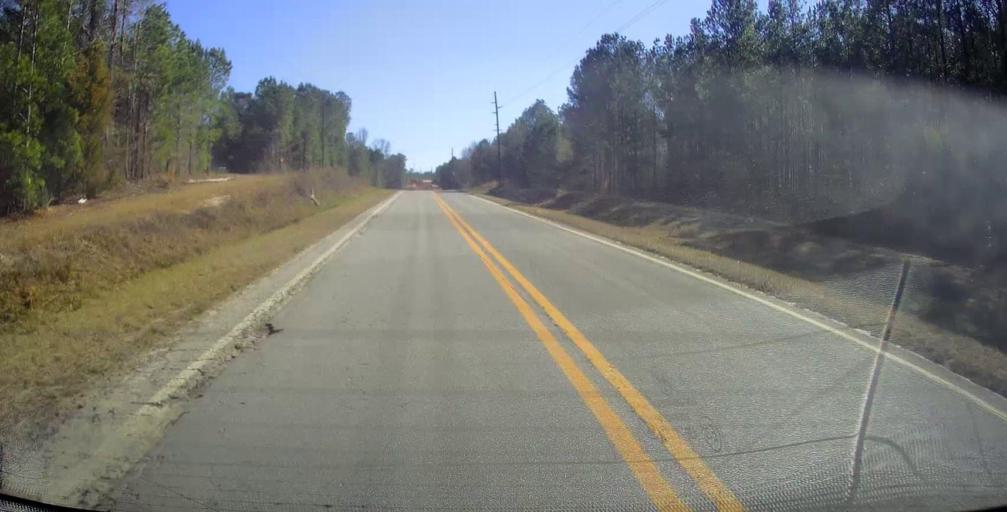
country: US
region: Georgia
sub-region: Crawford County
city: Roberta
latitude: 32.6432
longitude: -84.0049
